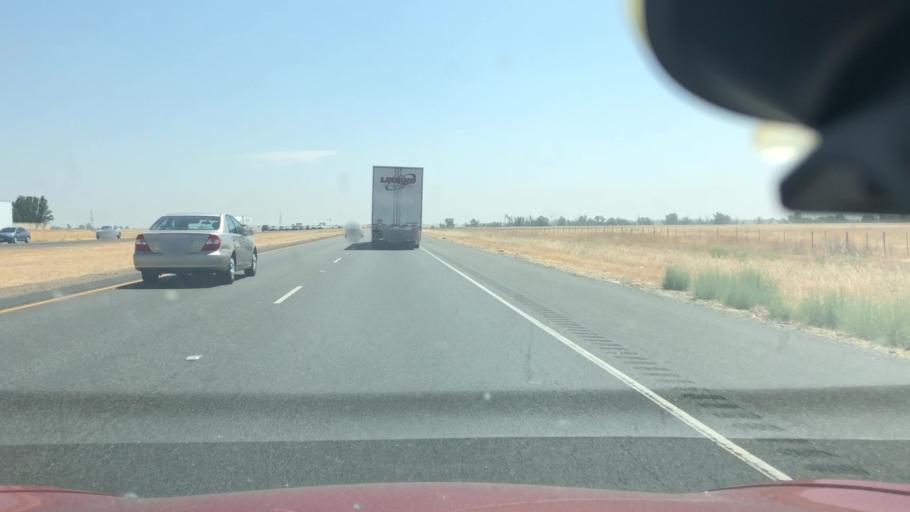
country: US
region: California
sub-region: Sacramento County
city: Laguna
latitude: 38.3964
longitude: -121.4814
